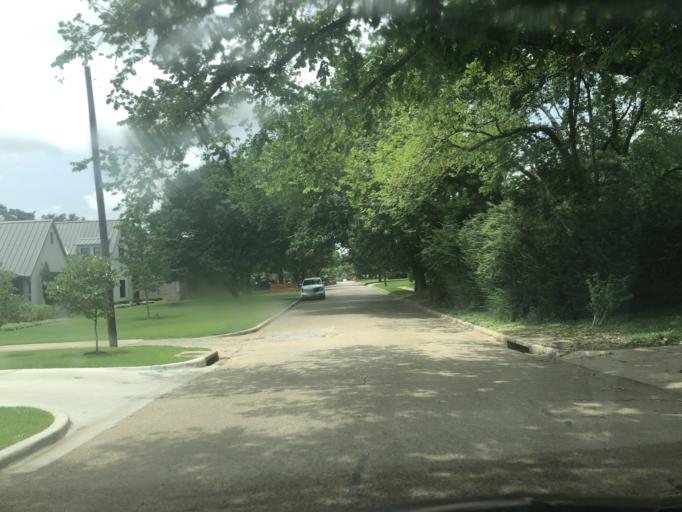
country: US
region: Texas
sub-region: Dallas County
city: University Park
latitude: 32.8690
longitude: -96.8417
